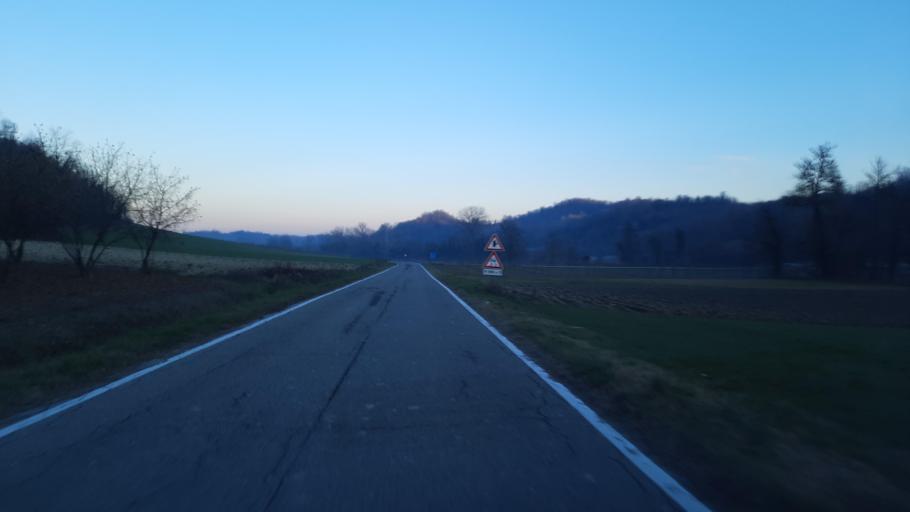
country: IT
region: Piedmont
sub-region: Provincia di Alessandria
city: Camino
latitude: 45.1505
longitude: 8.2745
